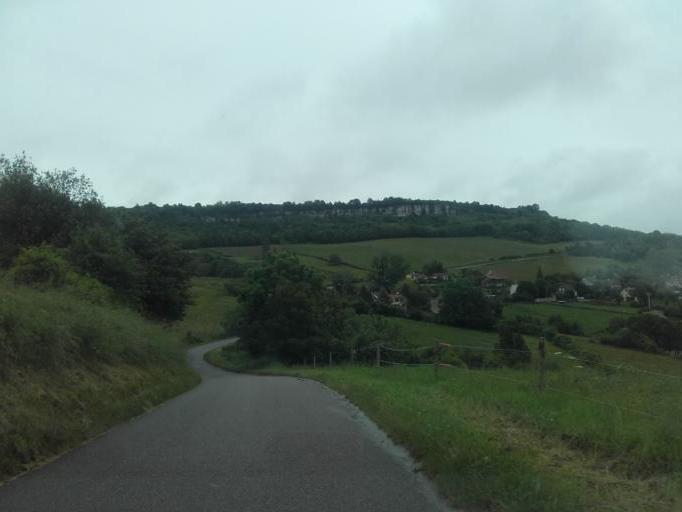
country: FR
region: Bourgogne
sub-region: Departement de la Cote-d'Or
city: Nolay
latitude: 46.9722
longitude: 4.6821
